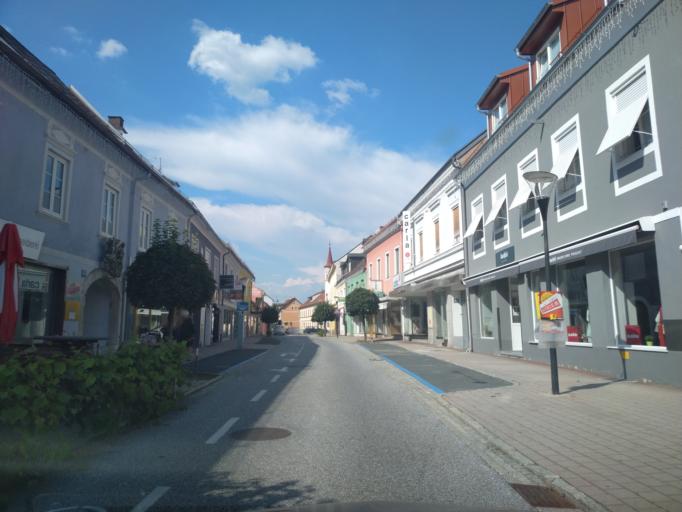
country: AT
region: Styria
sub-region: Politischer Bezirk Leibnitz
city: Leibnitz
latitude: 46.7828
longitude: 15.5390
